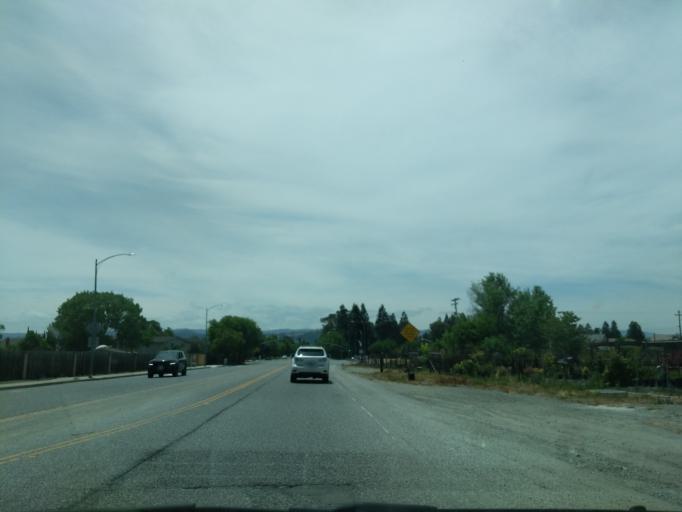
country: US
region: California
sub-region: Santa Clara County
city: Morgan Hill
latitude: 37.1393
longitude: -121.6133
